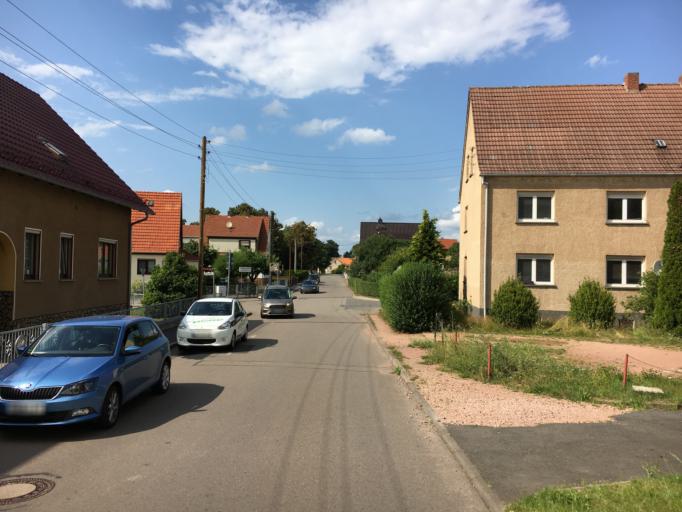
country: DE
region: Thuringia
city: Barchfeld
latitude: 50.7976
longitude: 10.3045
